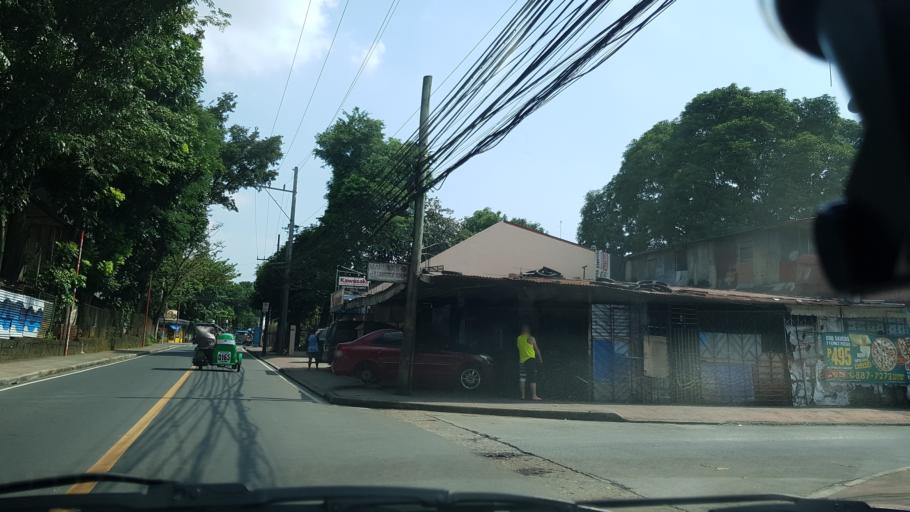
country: PH
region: Calabarzon
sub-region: Province of Rizal
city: San Mateo
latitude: 14.6637
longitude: 121.1118
